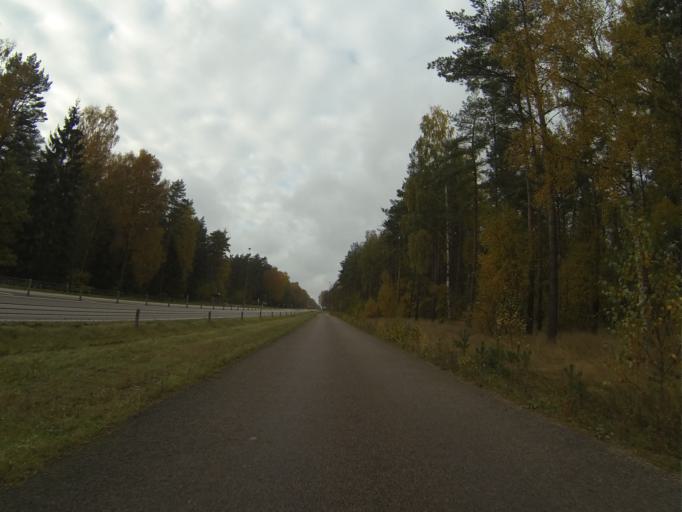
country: SE
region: Skane
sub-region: Sjobo Kommun
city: Sjoebo
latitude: 55.6373
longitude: 13.6572
